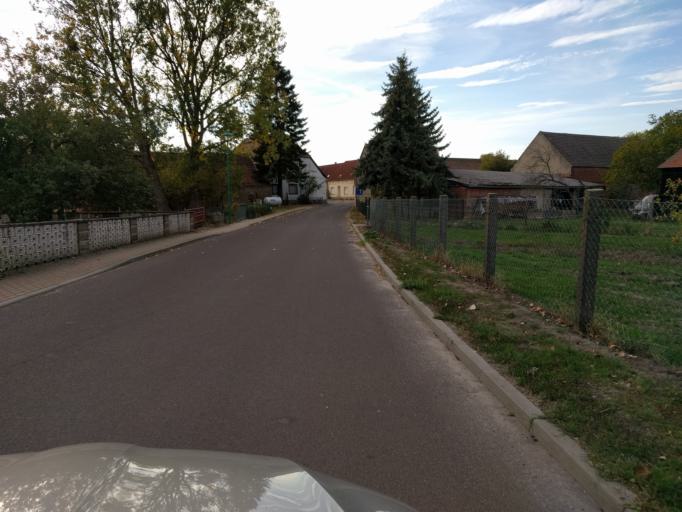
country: DE
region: Brandenburg
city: Ziesar
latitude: 52.2136
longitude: 12.2879
